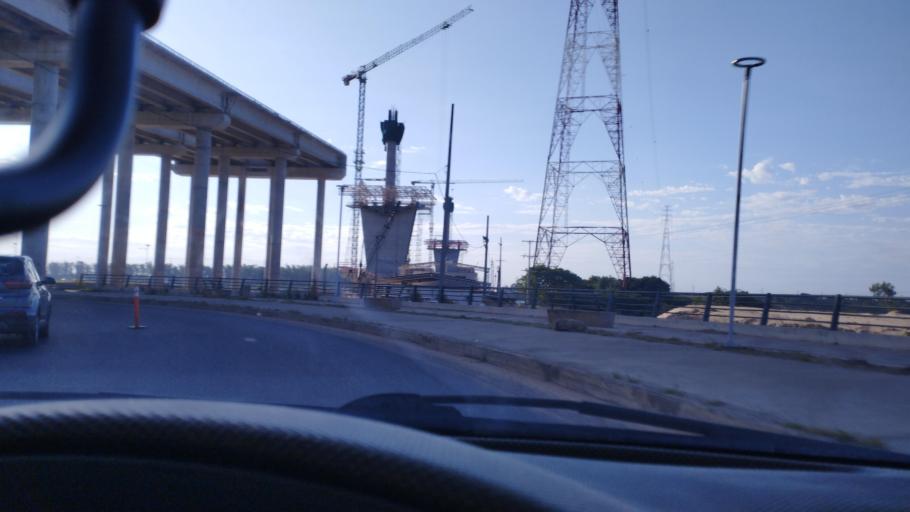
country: PY
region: Asuncion
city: Asuncion
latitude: -25.2441
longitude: -57.5899
